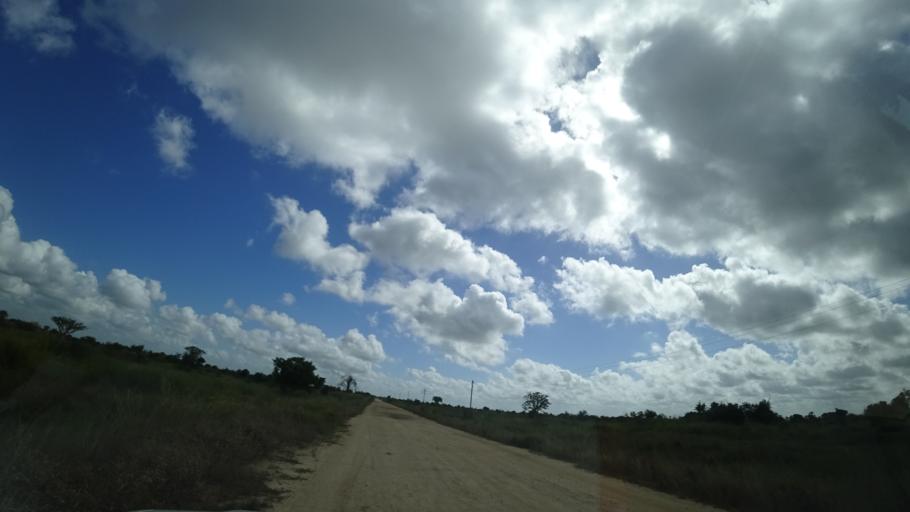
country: MZ
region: Sofala
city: Dondo
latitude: -19.4356
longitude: 34.5612
